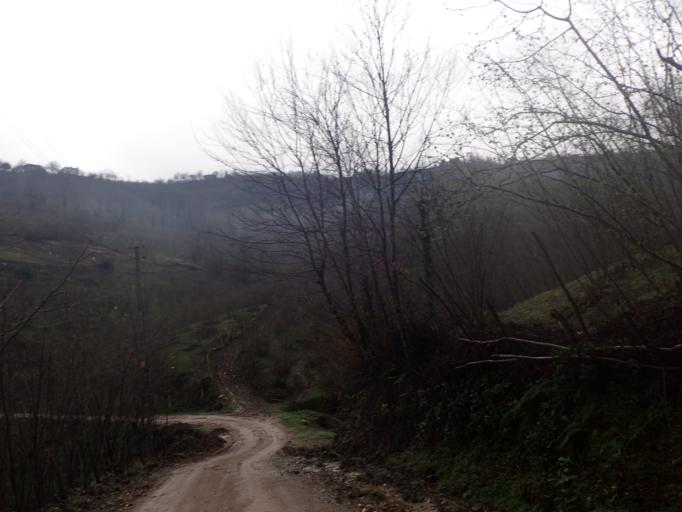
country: TR
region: Ordu
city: Camas
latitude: 40.9250
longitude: 37.5120
